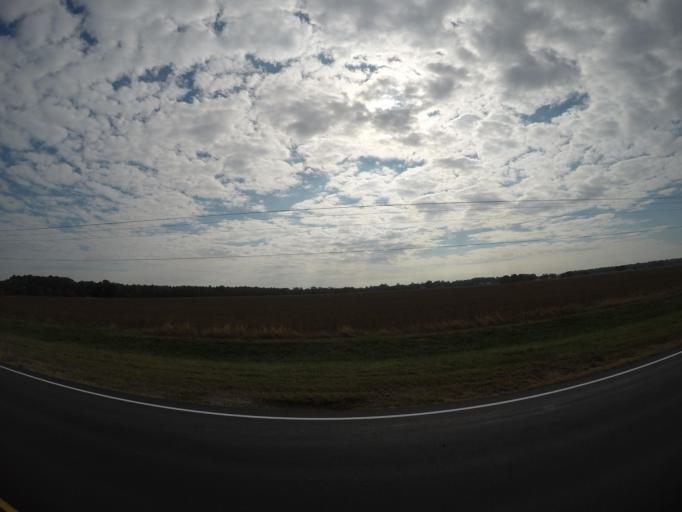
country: US
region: Delaware
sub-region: Sussex County
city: Bridgeville
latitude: 38.7575
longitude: -75.6240
